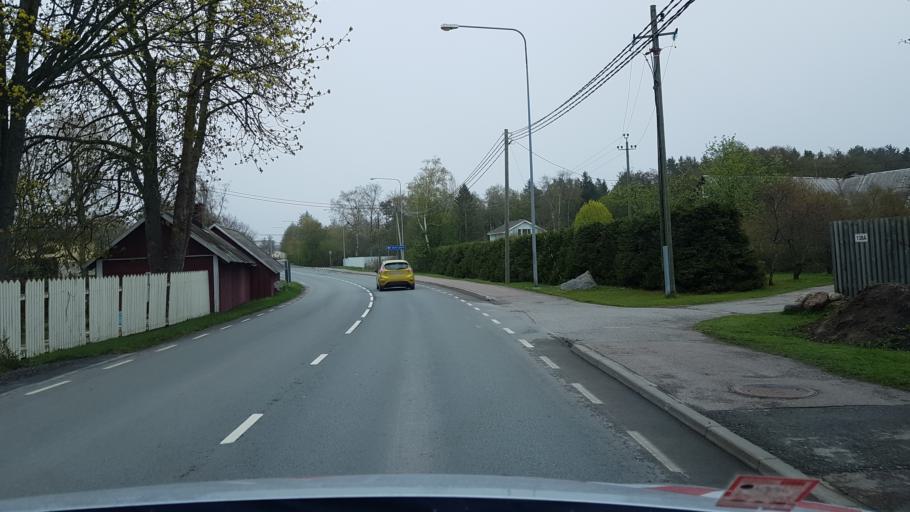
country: EE
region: Harju
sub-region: Viimsi vald
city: Rummu
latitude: 59.5575
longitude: 24.7969
